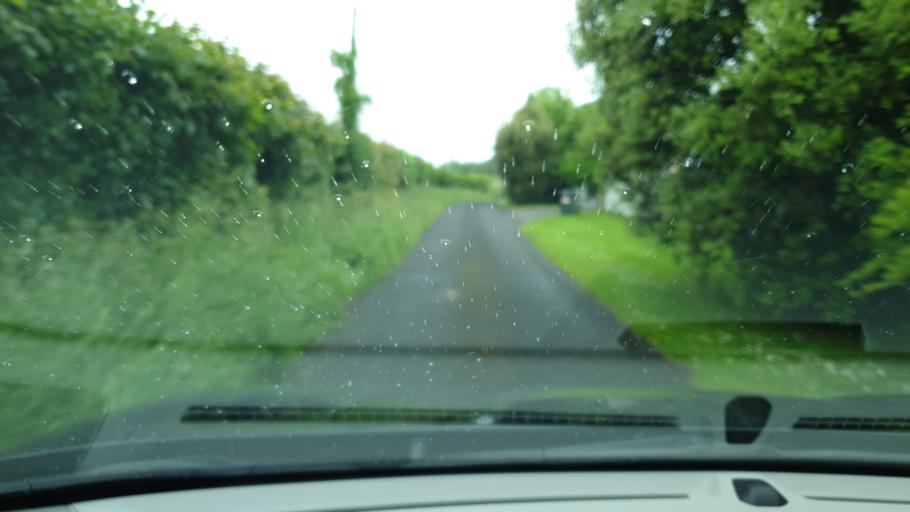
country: IE
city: Confey
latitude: 53.4317
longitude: -6.5305
